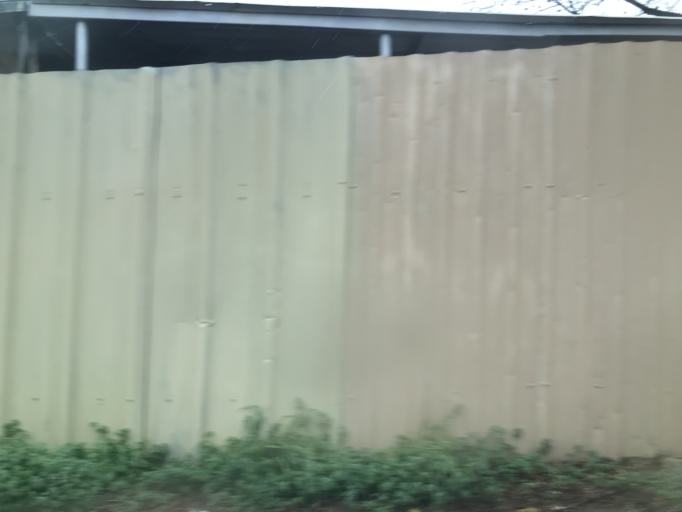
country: US
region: Texas
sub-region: Tom Green County
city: San Angelo
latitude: 31.4663
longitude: -100.4189
